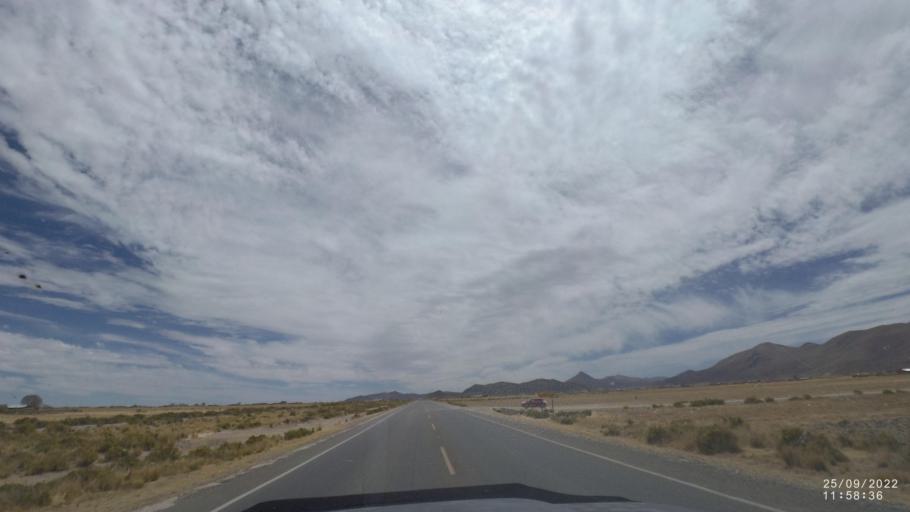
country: BO
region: Oruro
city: Challapata
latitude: -18.8018
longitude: -66.8388
